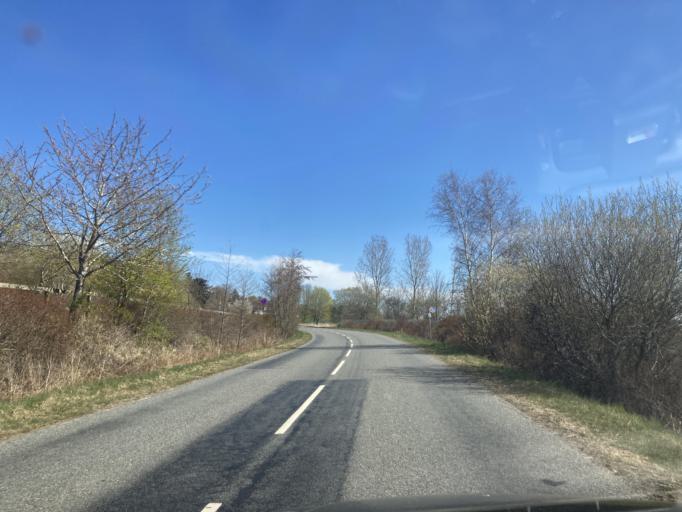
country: DK
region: Capital Region
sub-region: Gribskov Kommune
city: Helsinge
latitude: 56.0815
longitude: 12.1936
